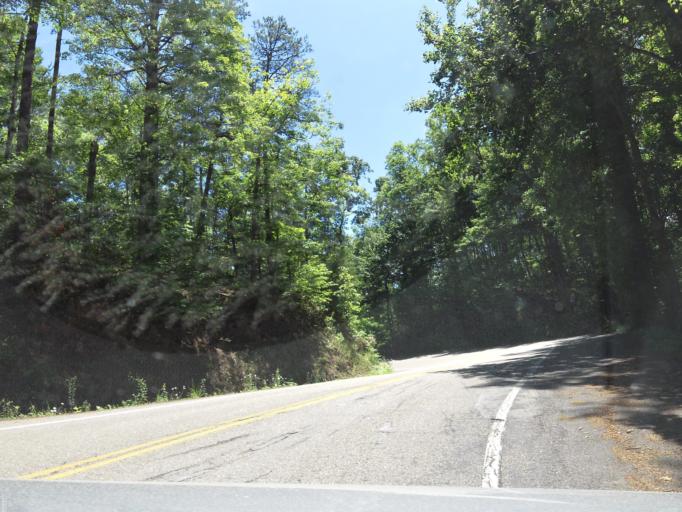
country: US
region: North Carolina
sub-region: Graham County
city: Robbinsville
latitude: 35.5045
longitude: -83.9559
